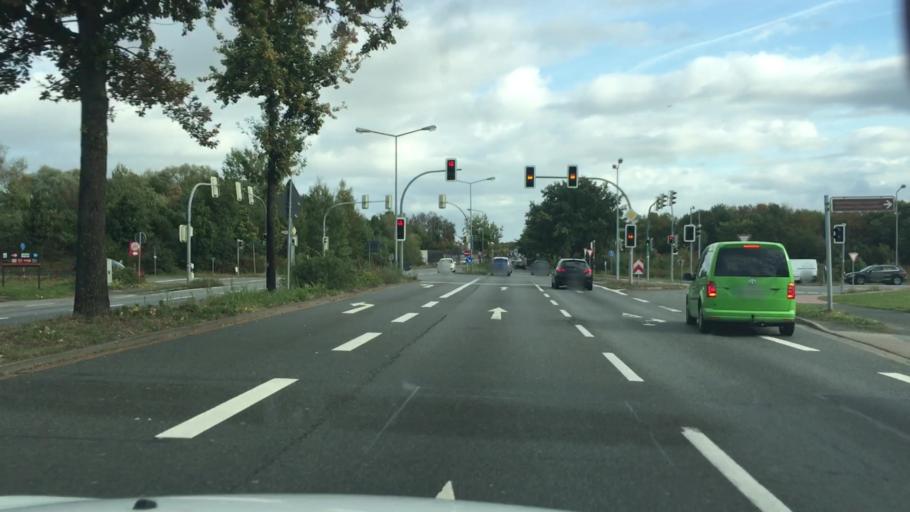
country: DE
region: Lower Saxony
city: Garbsen-Mitte
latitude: 52.4394
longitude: 9.5889
